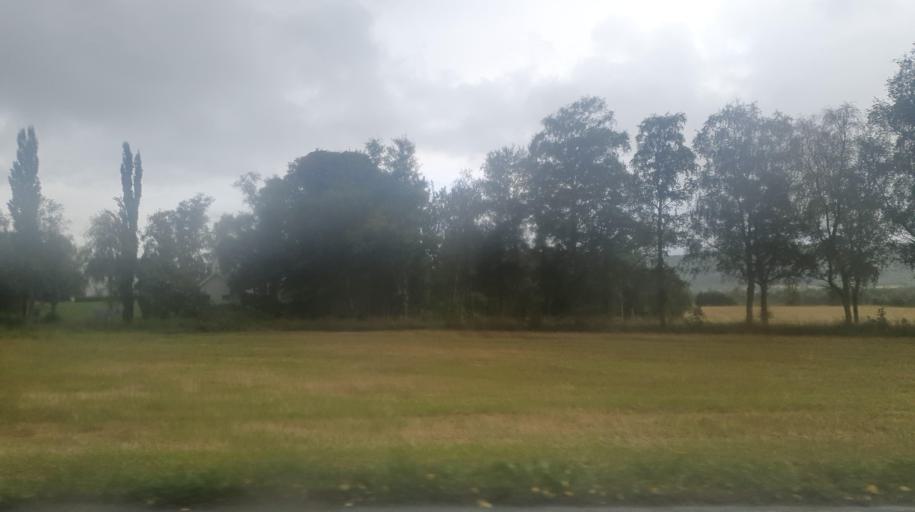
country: NO
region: Nord-Trondelag
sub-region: Verdal
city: Verdal
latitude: 63.7945
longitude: 11.5509
